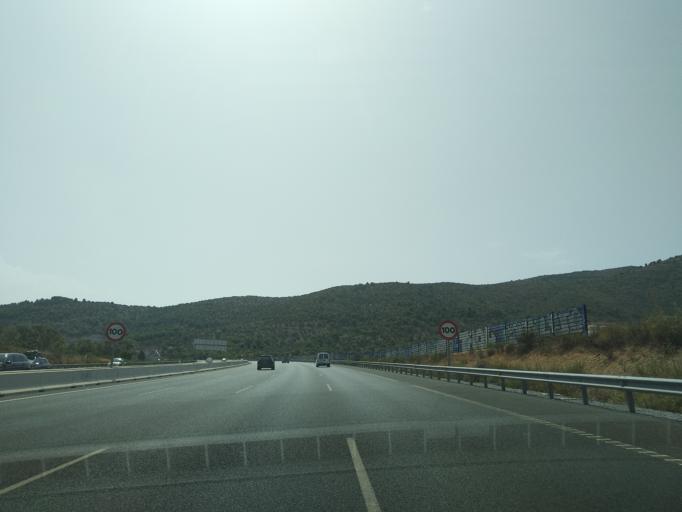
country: ES
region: Andalusia
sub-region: Provincia de Malaga
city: Alhaurin de la Torre
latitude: 36.6646
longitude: -4.5287
